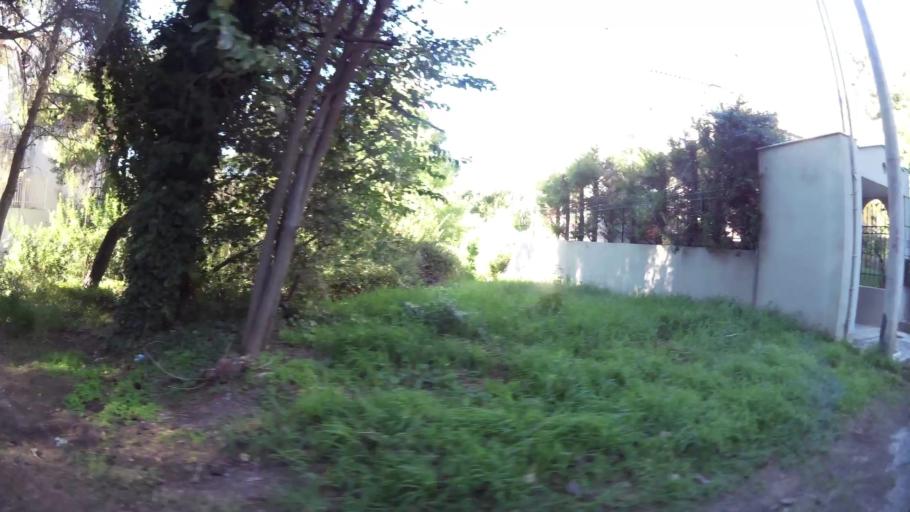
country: GR
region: Attica
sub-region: Nomarchia Athinas
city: Ekali
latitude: 38.1241
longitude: 23.8420
